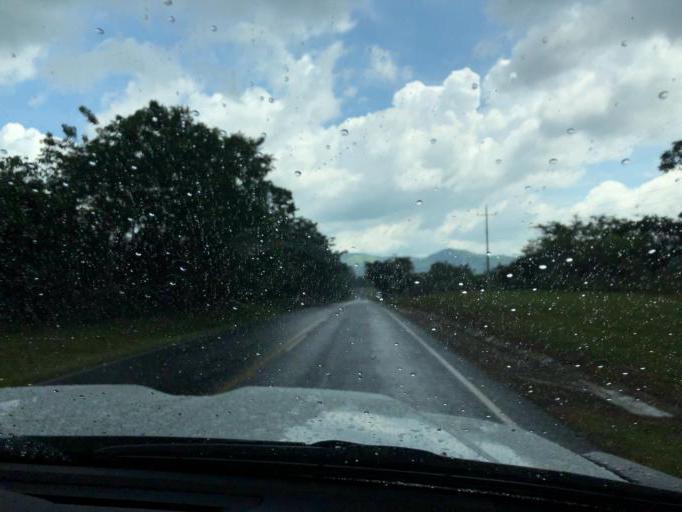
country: NI
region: Chontales
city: Villa Sandino
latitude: 12.0125
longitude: -84.9470
